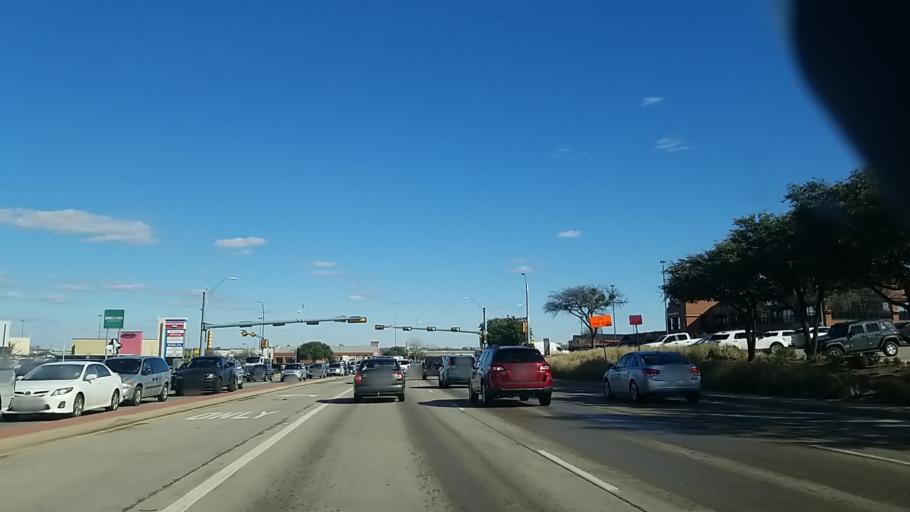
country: US
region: Texas
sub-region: Denton County
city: Denton
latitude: 33.1875
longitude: -97.1068
